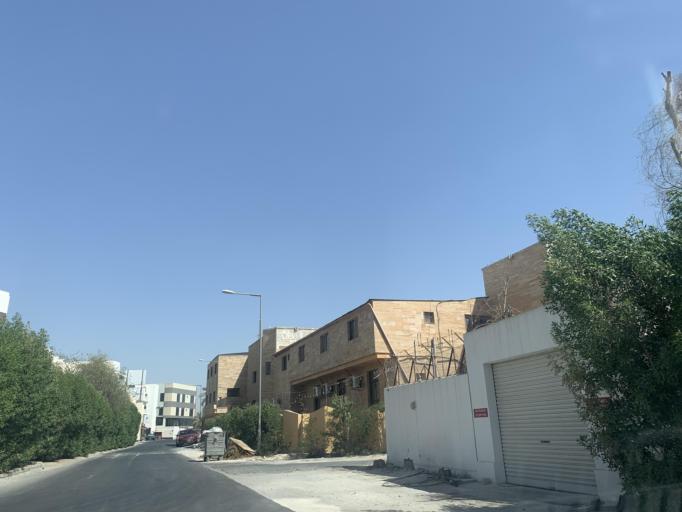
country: BH
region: Manama
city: Jidd Hafs
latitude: 26.2222
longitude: 50.5013
